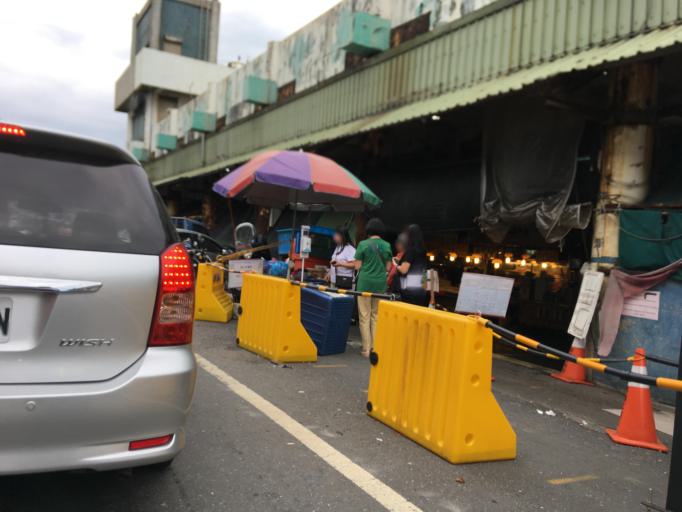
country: TW
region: Taiwan
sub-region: Yilan
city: Yilan
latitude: 24.5813
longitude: 121.8700
